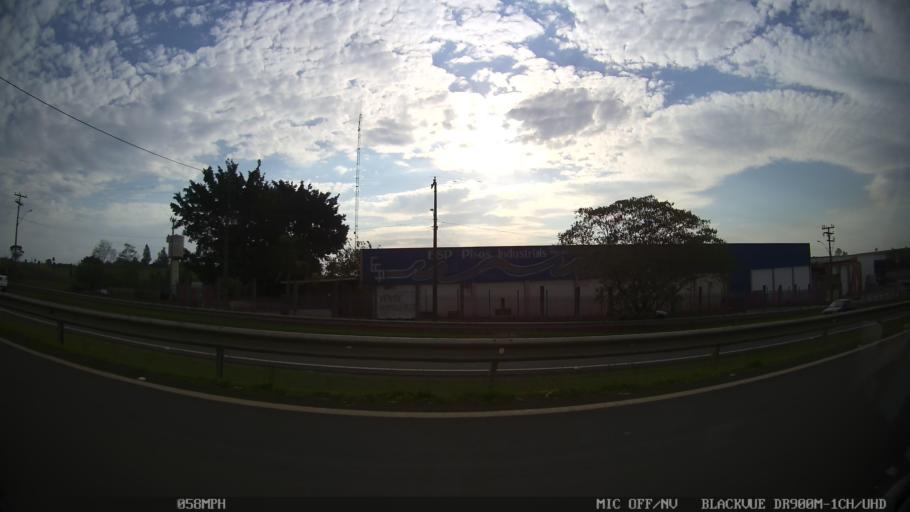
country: BR
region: Sao Paulo
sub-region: Cosmopolis
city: Cosmopolis
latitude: -22.6291
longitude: -47.2039
